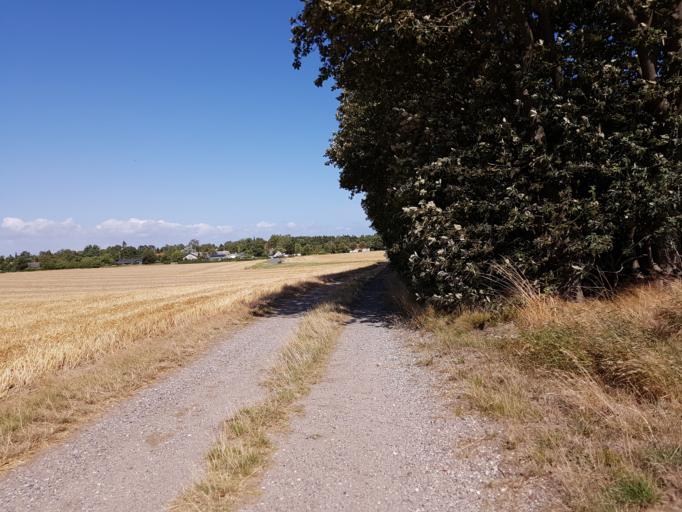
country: DK
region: Zealand
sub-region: Guldborgsund Kommune
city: Nykobing Falster
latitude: 54.5976
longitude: 11.9409
